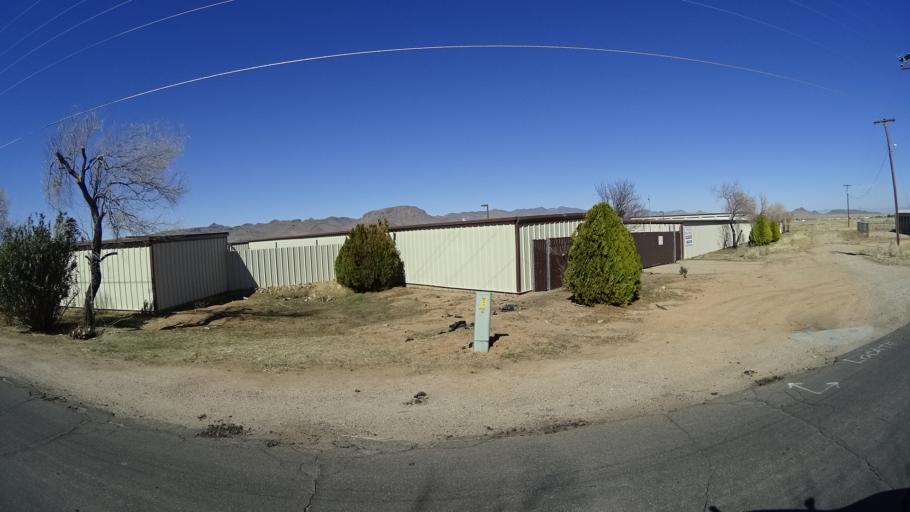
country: US
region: Arizona
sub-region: Mohave County
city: New Kingman-Butler
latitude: 35.2337
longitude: -113.9982
